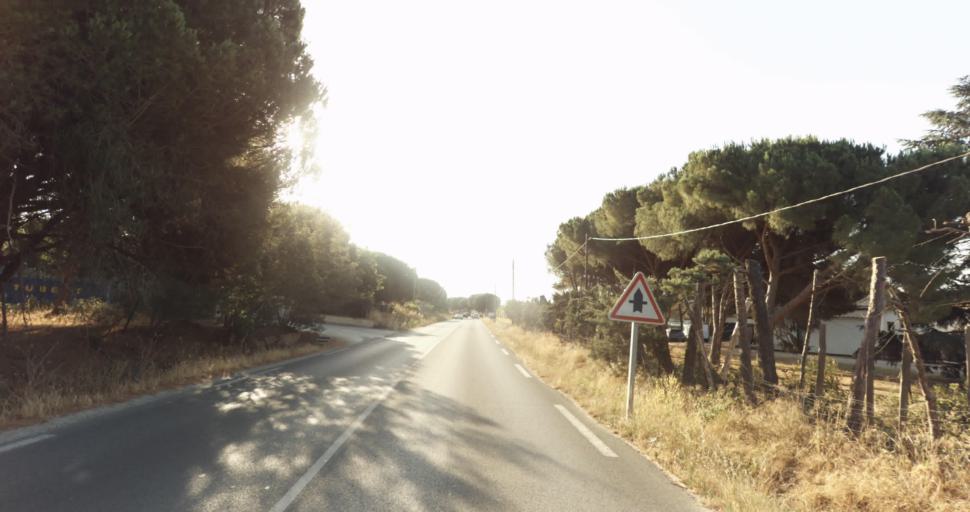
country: FR
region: Languedoc-Roussillon
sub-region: Departement des Pyrenees-Orientales
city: Latour-Bas-Elne
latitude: 42.6070
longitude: 2.9914
